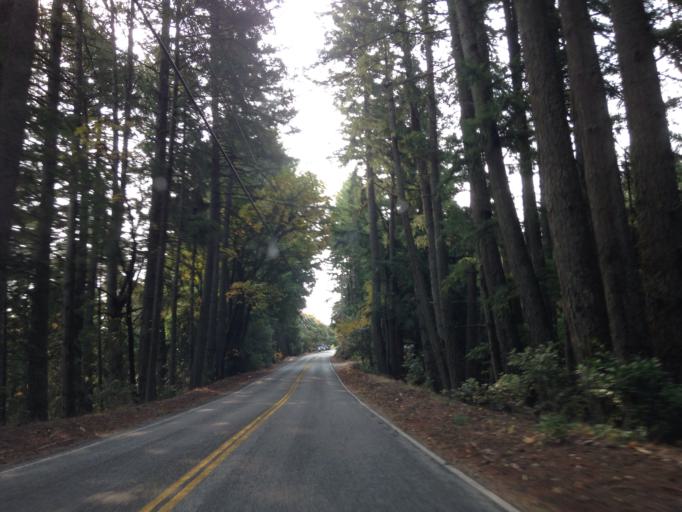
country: US
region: California
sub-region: San Mateo County
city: Woodside
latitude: 37.4130
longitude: -122.3075
